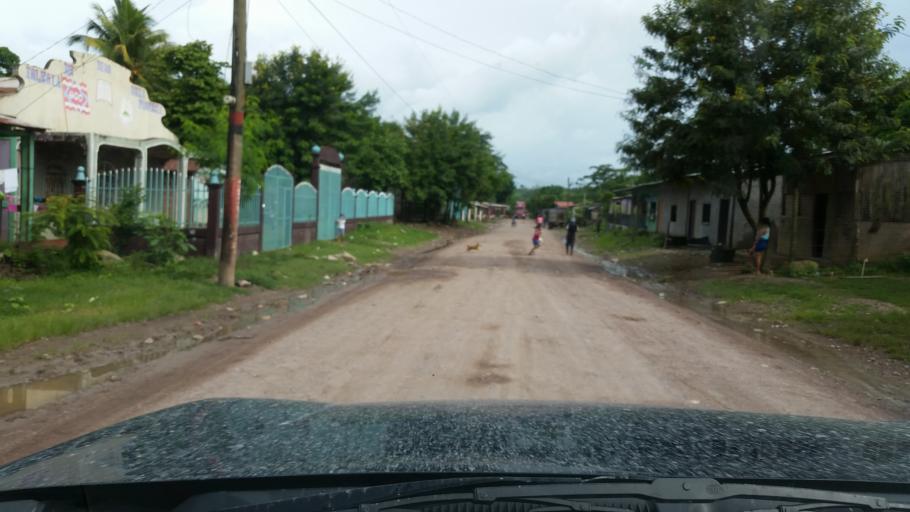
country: NI
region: Atlantico Norte (RAAN)
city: Siuna
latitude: 13.4809
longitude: -84.8442
